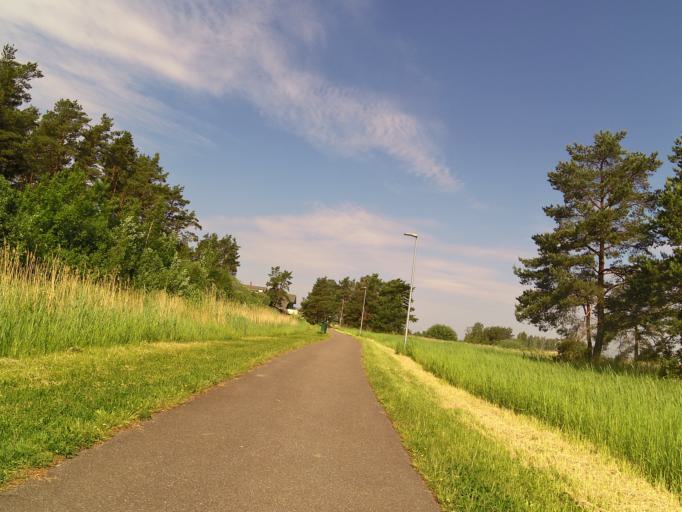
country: EE
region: Laeaene
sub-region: Haapsalu linn
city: Haapsalu
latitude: 58.9398
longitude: 23.5205
